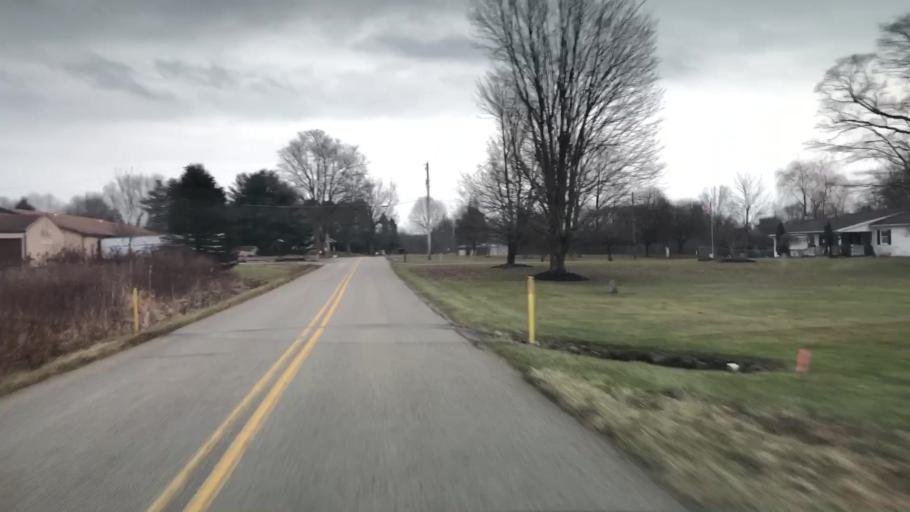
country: US
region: Pennsylvania
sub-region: Mercer County
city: Grove City
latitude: 41.1333
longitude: -80.1221
